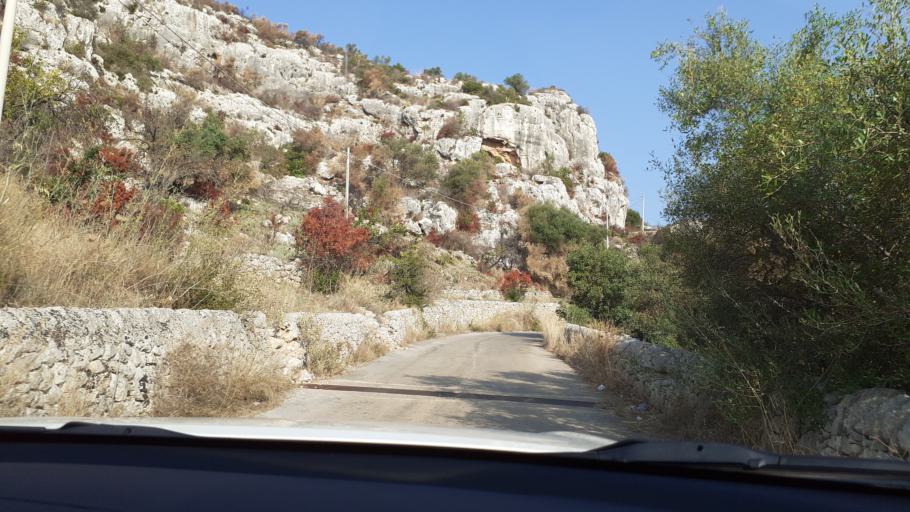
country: IT
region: Sicily
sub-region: Provincia di Siracusa
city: Cassibile
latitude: 36.9793
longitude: 15.1719
